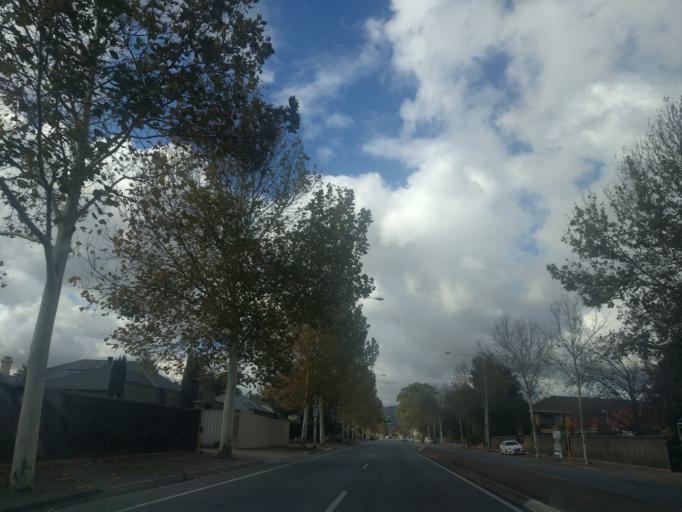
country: AU
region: South Australia
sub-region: Unley
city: Unley Park
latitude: -34.9656
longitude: 138.6043
